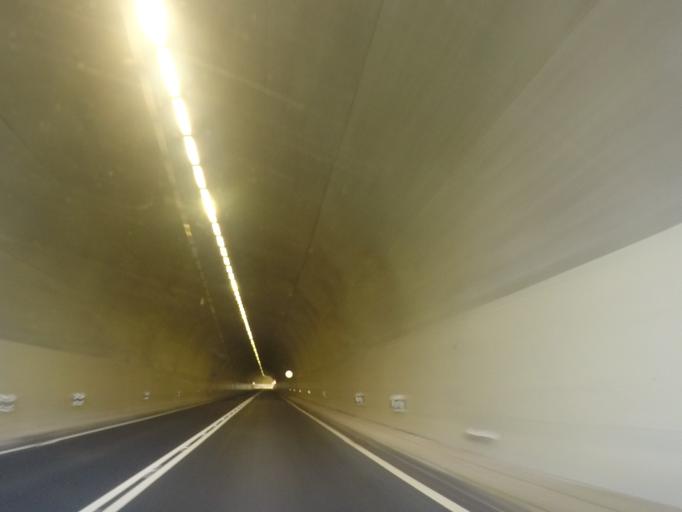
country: PT
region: Madeira
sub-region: Calheta
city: Faja da Ovelha
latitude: 32.7949
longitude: -17.2326
